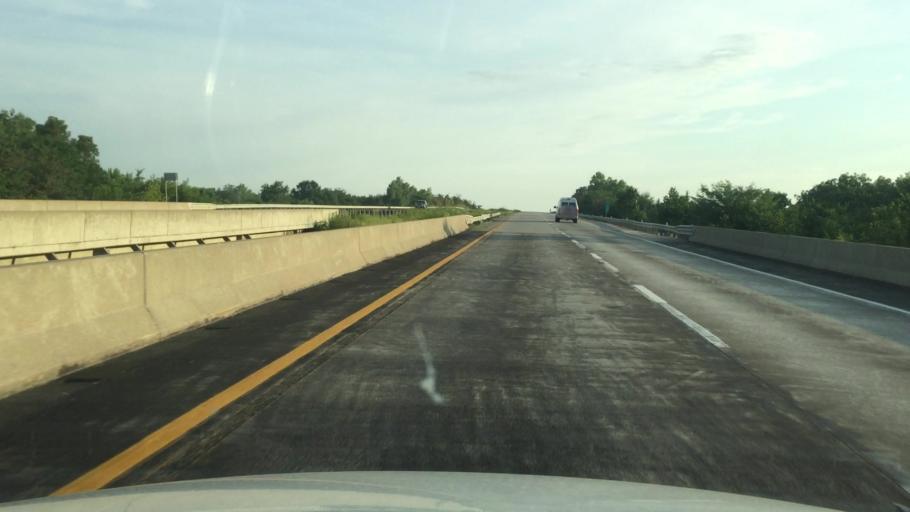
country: US
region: Missouri
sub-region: Clinton County
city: Gower
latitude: 39.5720
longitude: -94.7884
